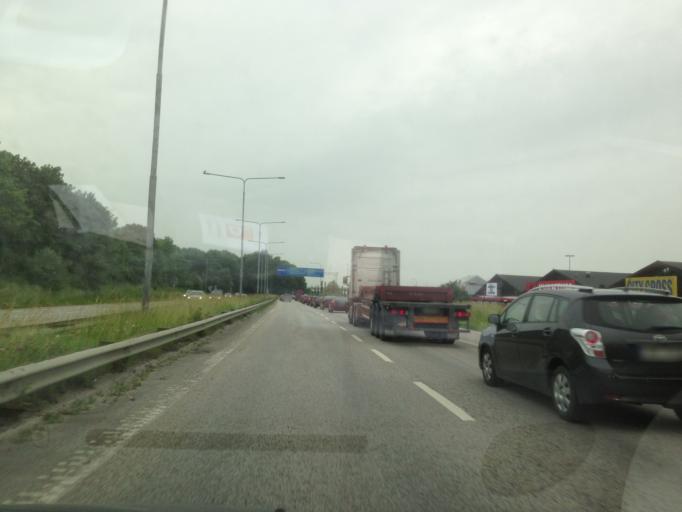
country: SE
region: Skane
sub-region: Lunds Kommun
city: Lund
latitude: 55.7172
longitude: 13.1664
